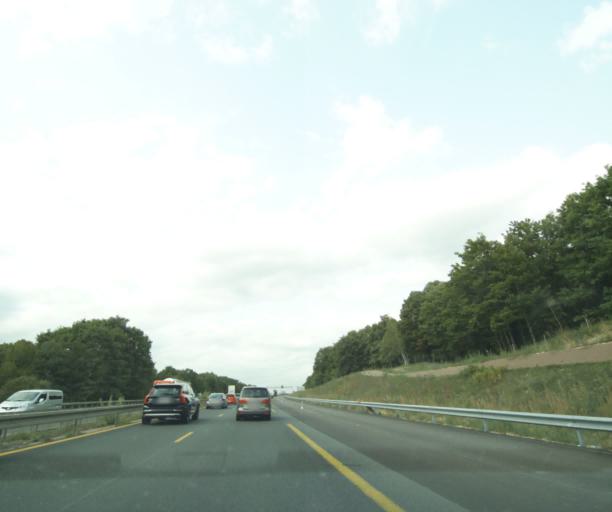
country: FR
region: Centre
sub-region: Departement d'Indre-et-Loire
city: Chambray-les-Tours
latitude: 47.3176
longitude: 0.6893
